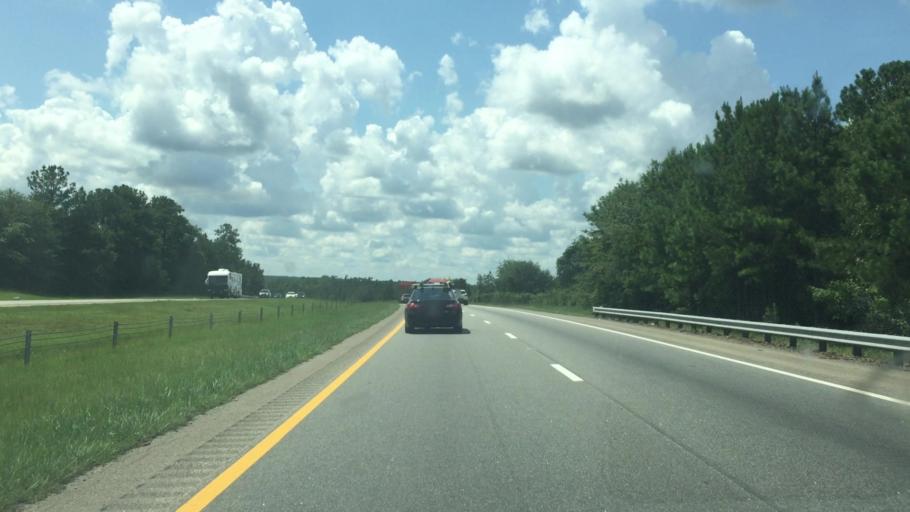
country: US
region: North Carolina
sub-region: Richmond County
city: Cordova
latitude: 34.8966
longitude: -79.7911
